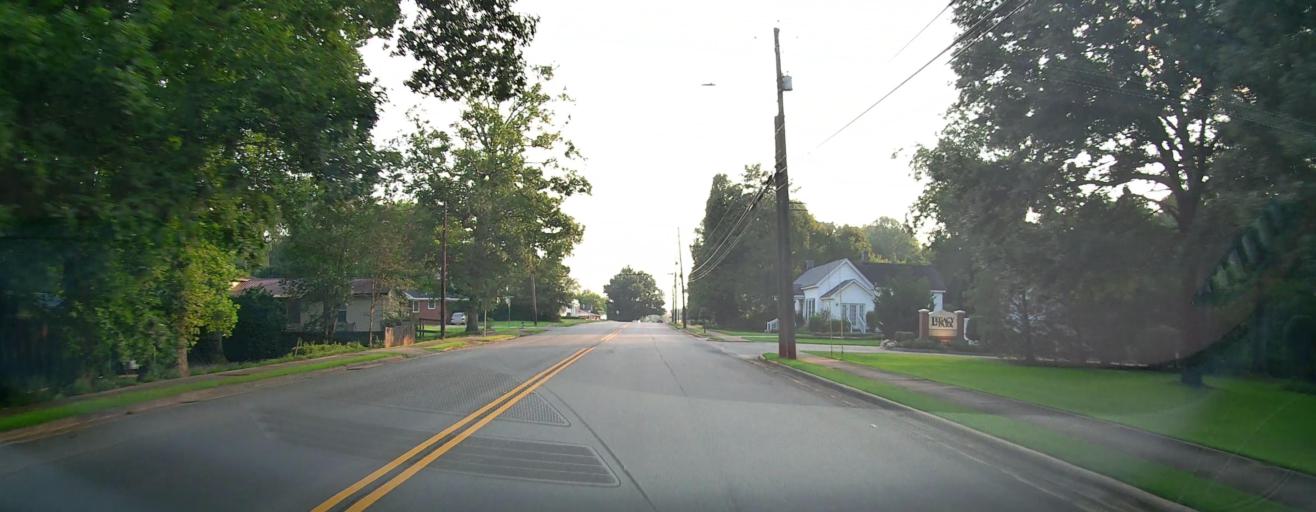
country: US
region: Georgia
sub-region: Jones County
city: Gray
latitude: 33.0117
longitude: -83.5293
